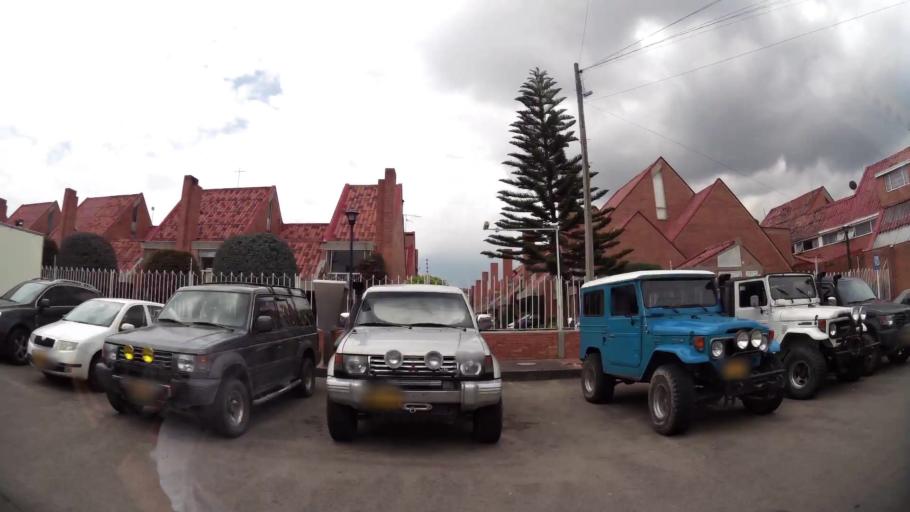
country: CO
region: Cundinamarca
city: Cota
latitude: 4.7661
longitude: -74.0421
